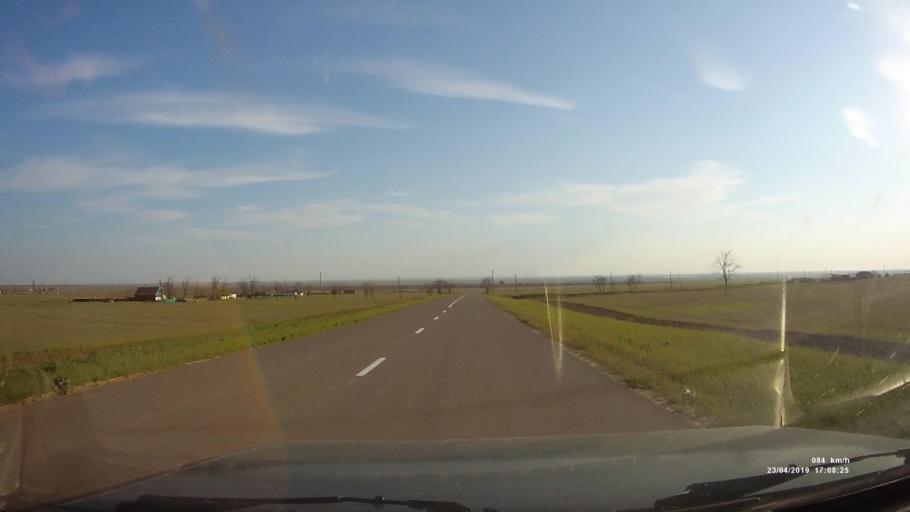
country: RU
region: Kalmykiya
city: Priyutnoye
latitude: 46.2721
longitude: 43.4882
